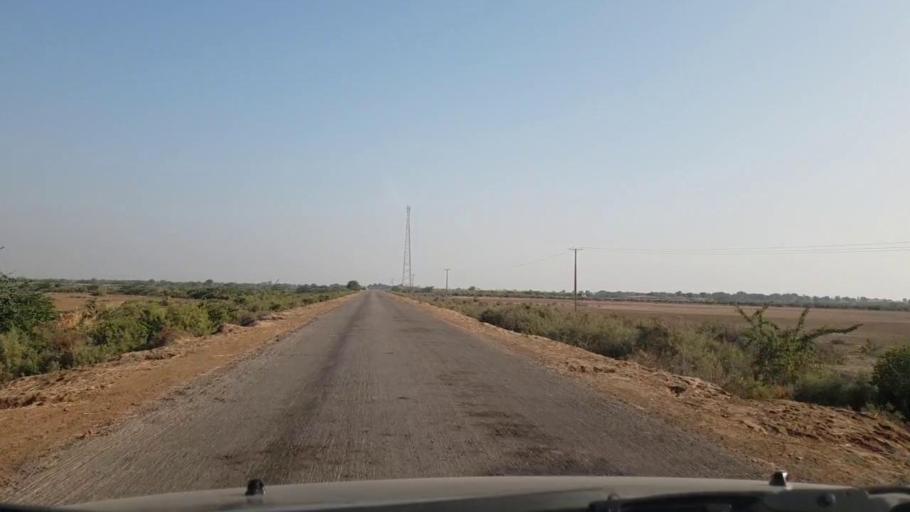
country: PK
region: Sindh
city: Tando Bago
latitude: 24.8527
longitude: 69.0386
